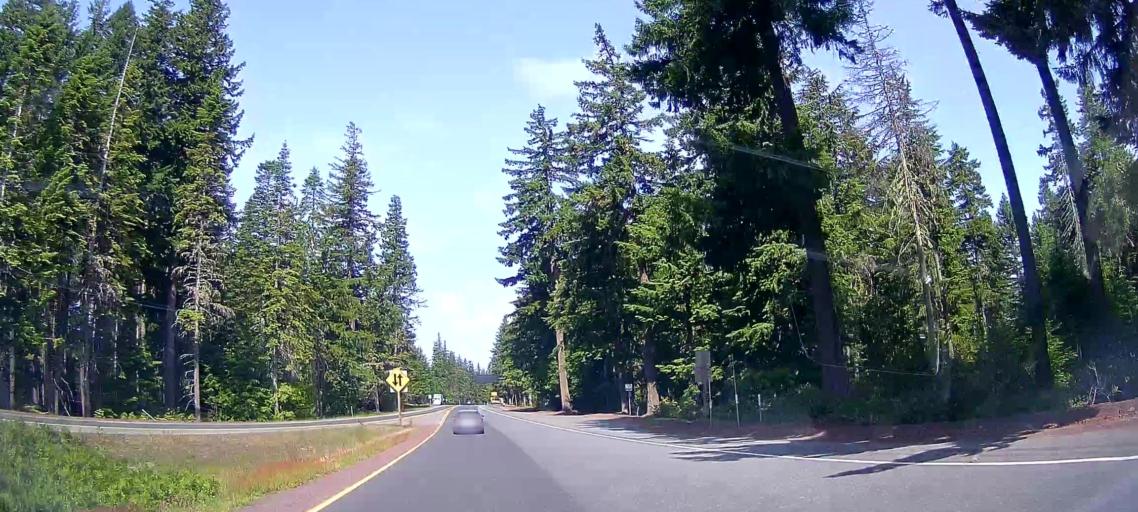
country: US
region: Oregon
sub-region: Clackamas County
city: Mount Hood Village
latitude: 45.1317
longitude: -121.6033
